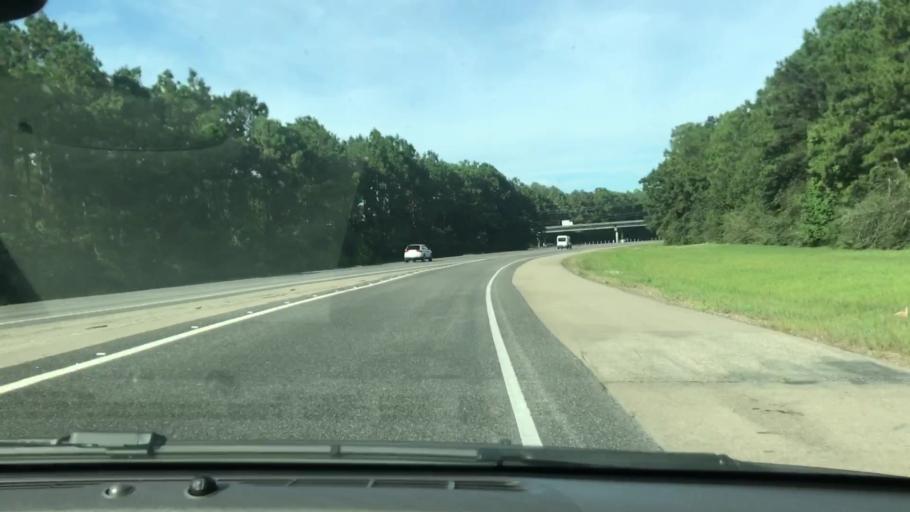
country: US
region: Louisiana
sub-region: Saint Tammany Parish
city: Slidell
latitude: 30.3076
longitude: -89.7400
